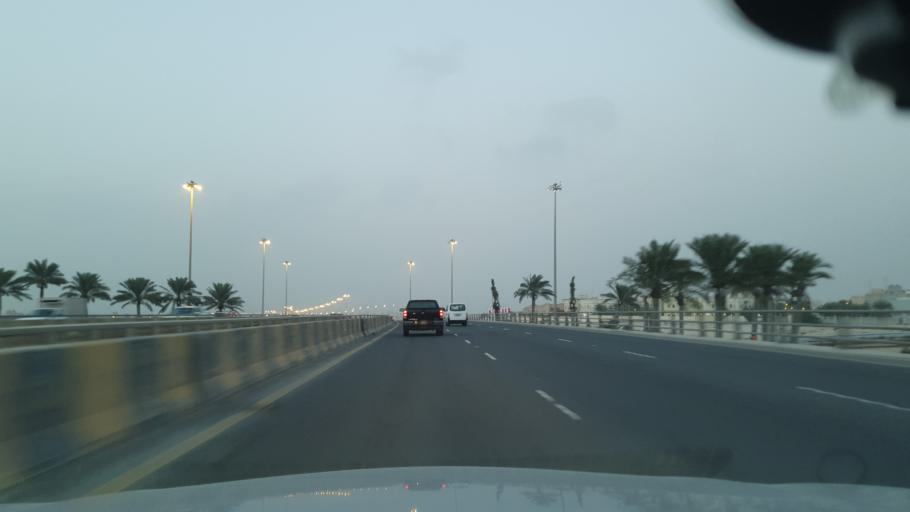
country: BH
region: Central Governorate
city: Madinat Hamad
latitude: 26.1387
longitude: 50.5101
